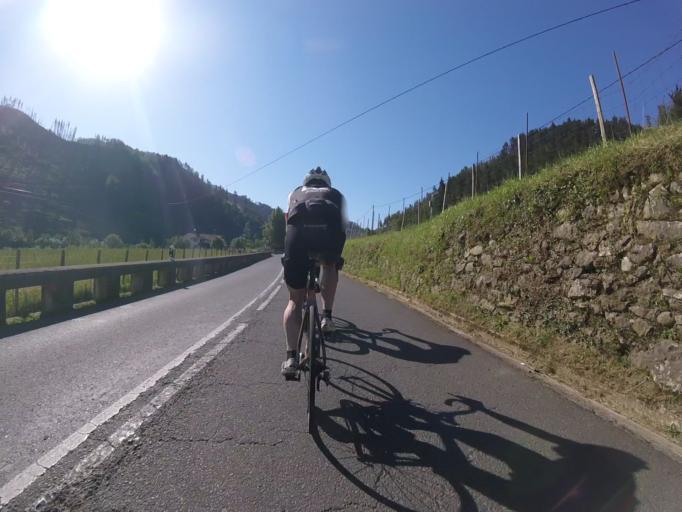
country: ES
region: Basque Country
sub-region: Provincia de Guipuzcoa
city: Azpeitia
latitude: 43.1522
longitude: -2.2403
